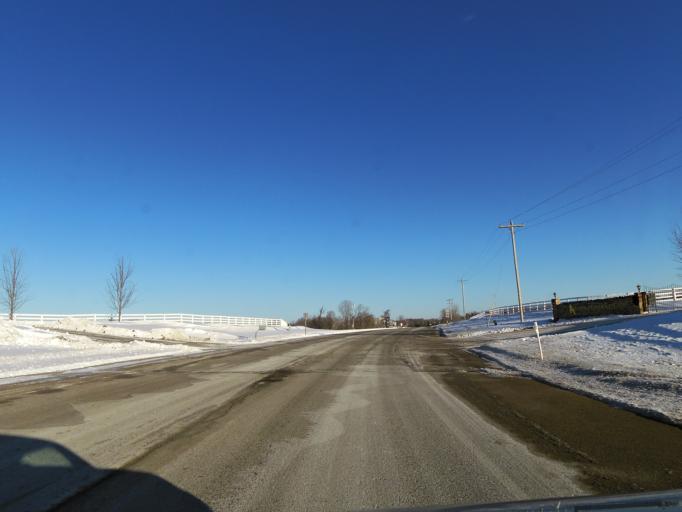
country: US
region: Minnesota
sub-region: Scott County
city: Jordan
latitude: 44.6613
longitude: -93.6135
